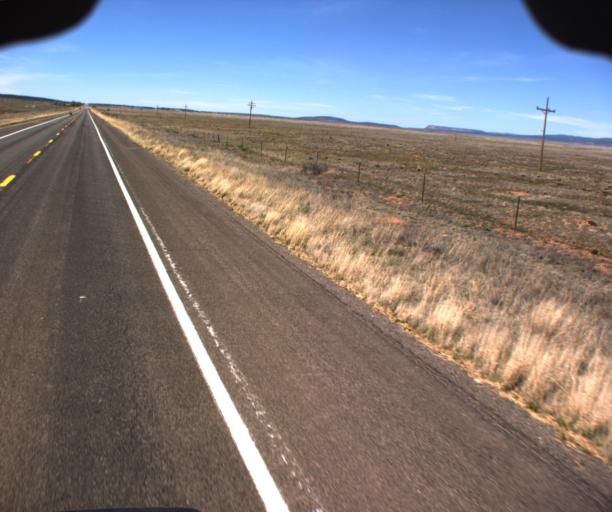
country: US
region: Arizona
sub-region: Mohave County
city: Peach Springs
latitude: 35.4681
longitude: -113.1215
